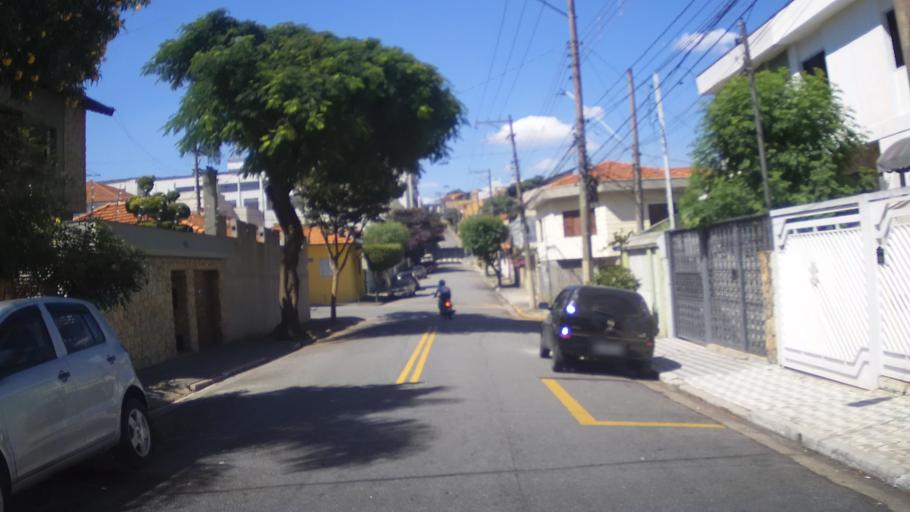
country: BR
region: Sao Paulo
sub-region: Sao Caetano Do Sul
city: Sao Caetano do Sul
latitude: -23.6292
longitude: -46.5707
